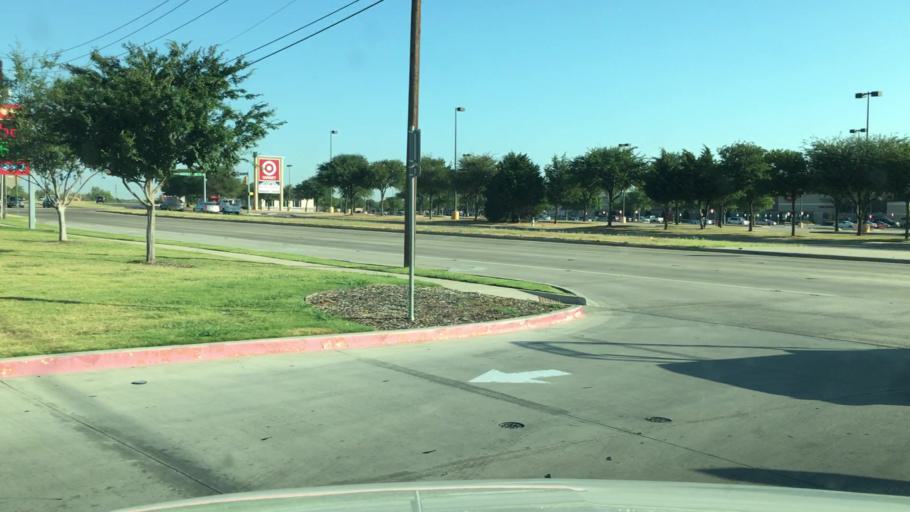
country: US
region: Texas
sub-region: Johnson County
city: Burleson
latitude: 32.5211
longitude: -97.3495
